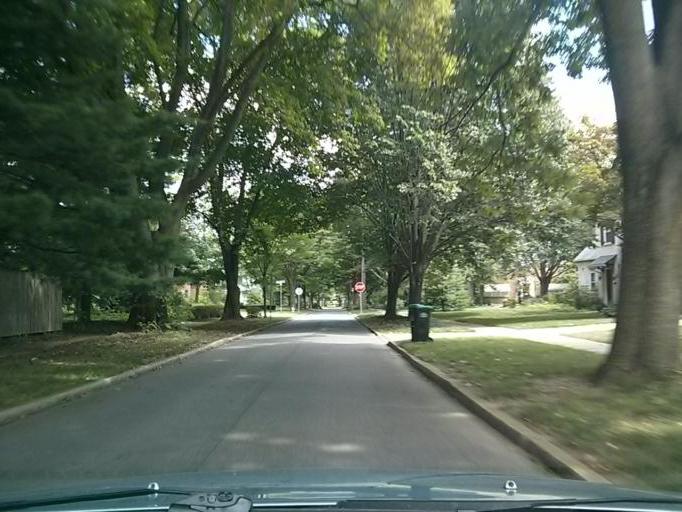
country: US
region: Pennsylvania
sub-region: Centre County
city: State College
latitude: 40.8019
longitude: -77.8699
